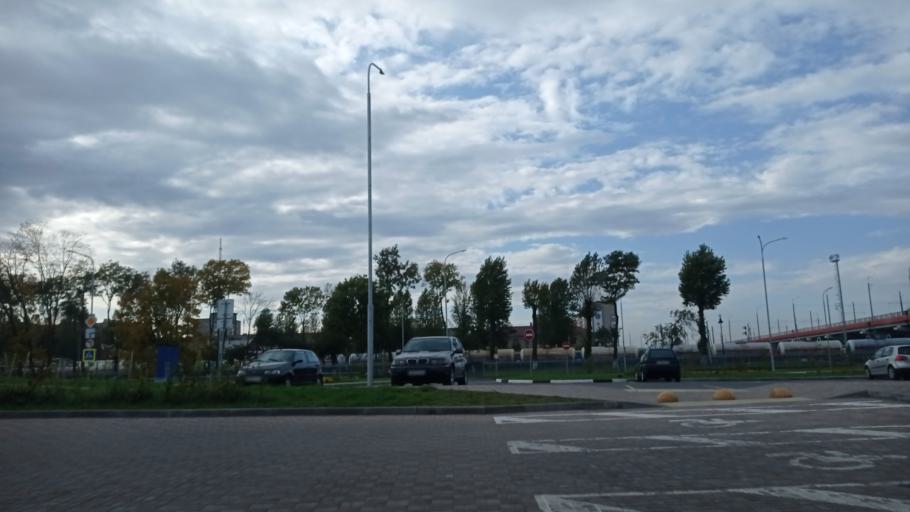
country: BY
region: Vitebsk
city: Vitebsk
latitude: 55.1978
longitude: 30.1879
